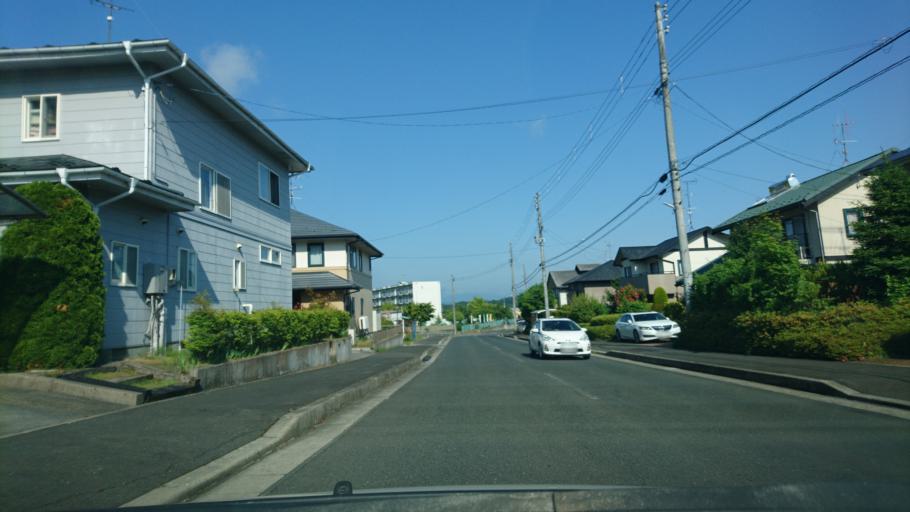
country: JP
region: Iwate
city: Ichinoseki
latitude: 38.9039
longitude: 141.1402
